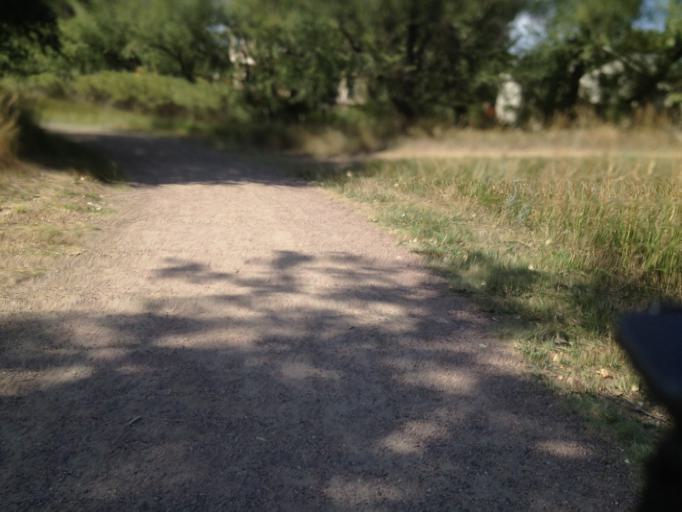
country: US
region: Colorado
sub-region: Boulder County
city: Louisville
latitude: 39.9920
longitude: -105.1204
